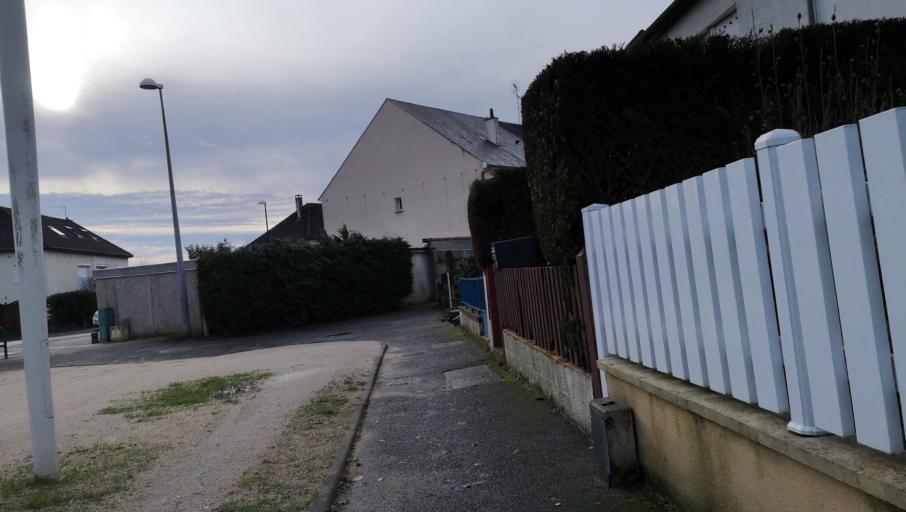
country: FR
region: Centre
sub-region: Departement du Loiret
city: Saint-Jean-de-Braye
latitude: 47.9225
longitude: 1.9639
